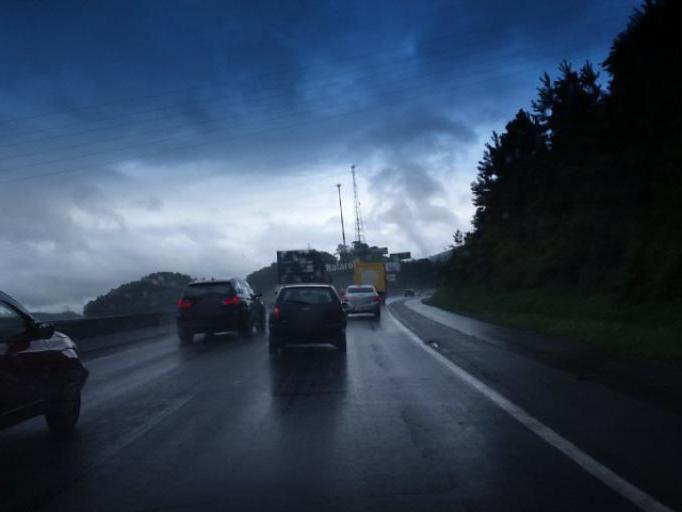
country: BR
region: Santa Catarina
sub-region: Balneario Camboriu
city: Balneario Camboriu
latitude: -26.9774
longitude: -48.6820
